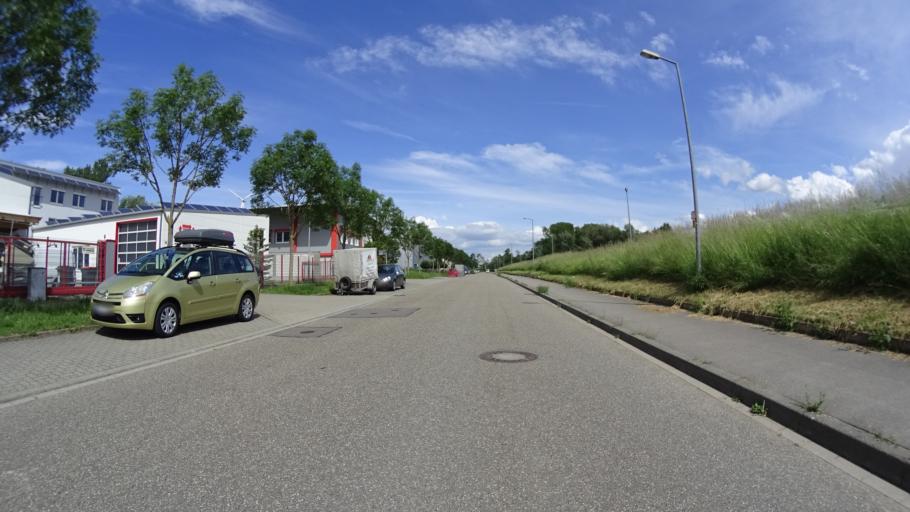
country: DE
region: Baden-Wuerttemberg
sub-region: Karlsruhe Region
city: Rheinstetten
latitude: 49.0180
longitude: 8.3235
